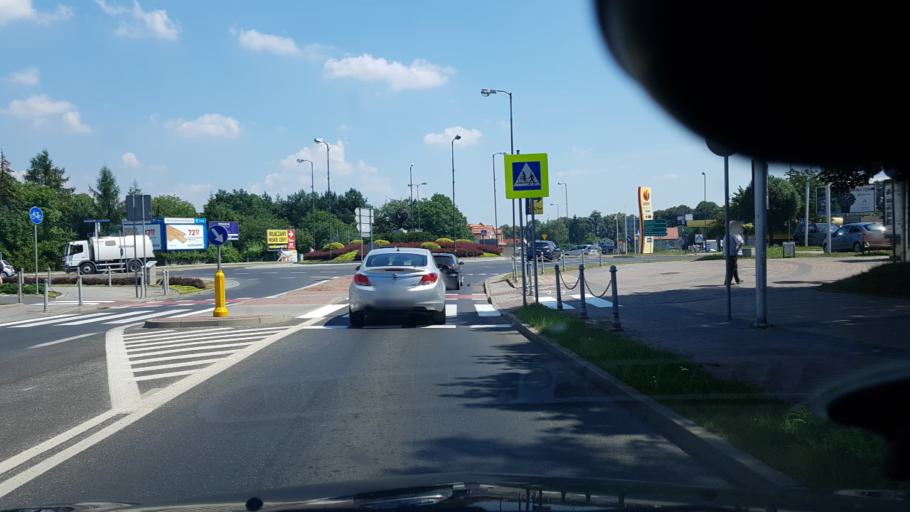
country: PL
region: Silesian Voivodeship
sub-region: Zory
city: Zory
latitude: 50.0428
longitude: 18.6889
